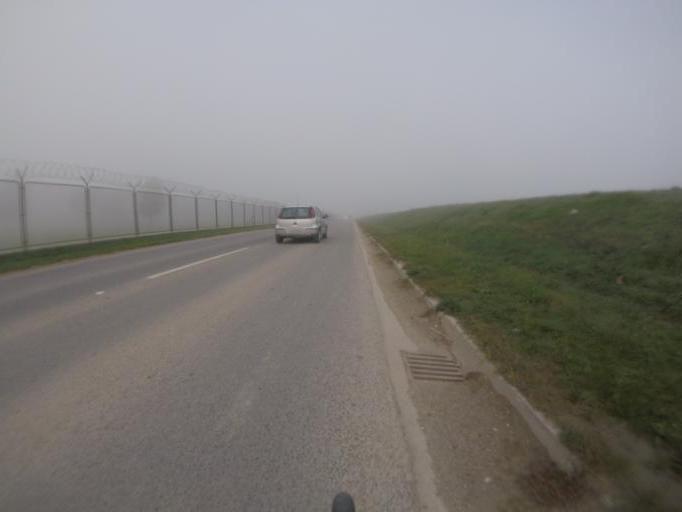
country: HR
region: Grad Zagreb
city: Novi Zagreb
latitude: 45.7738
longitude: 16.0170
